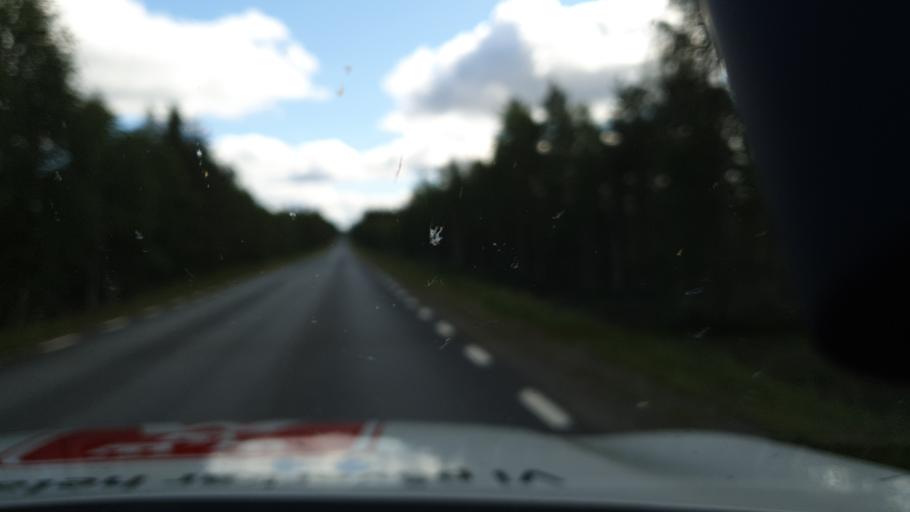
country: SE
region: Vaesterbotten
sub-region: Mala Kommun
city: Mala
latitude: 65.1478
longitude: 18.6061
